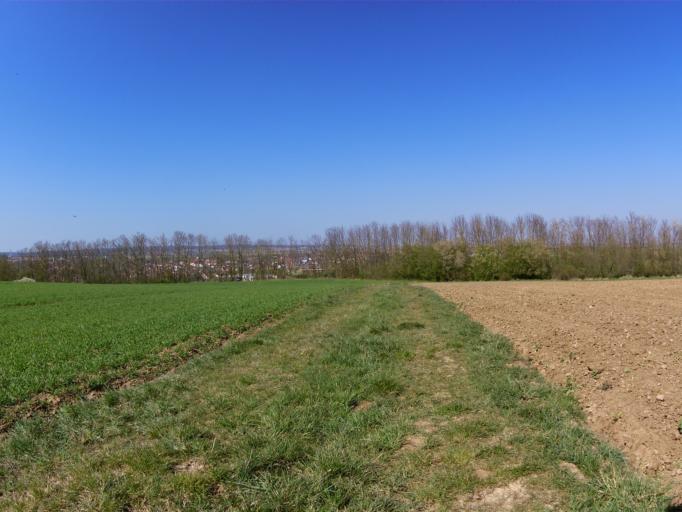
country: DE
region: Bavaria
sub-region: Regierungsbezirk Unterfranken
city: Kurnach
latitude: 49.8383
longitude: 10.0516
